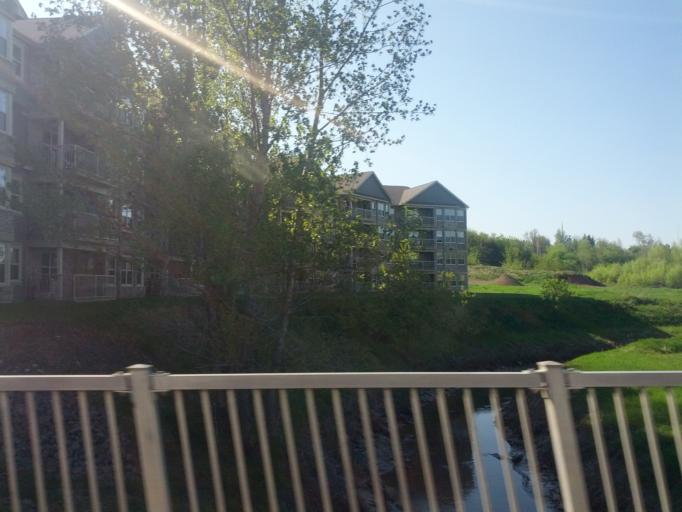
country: CA
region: New Brunswick
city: Moncton
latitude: 46.1022
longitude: -64.7702
